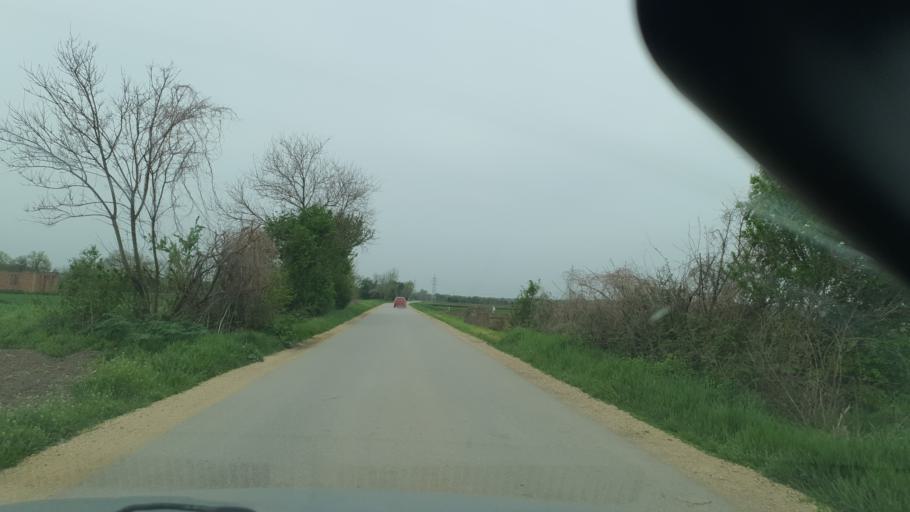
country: RS
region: Central Serbia
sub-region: Branicevski Okrug
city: Pozarevac
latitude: 44.7125
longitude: 21.1340
